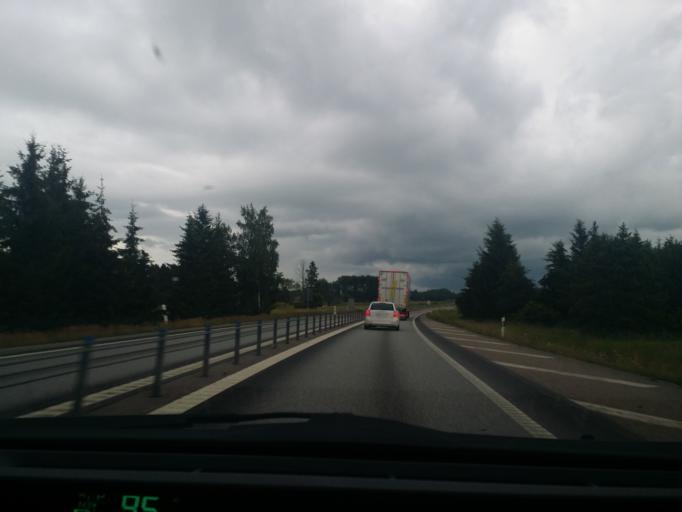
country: SE
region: Vaestmanland
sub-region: Hallstahammars Kommun
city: Kolback
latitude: 59.5925
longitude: 16.2492
